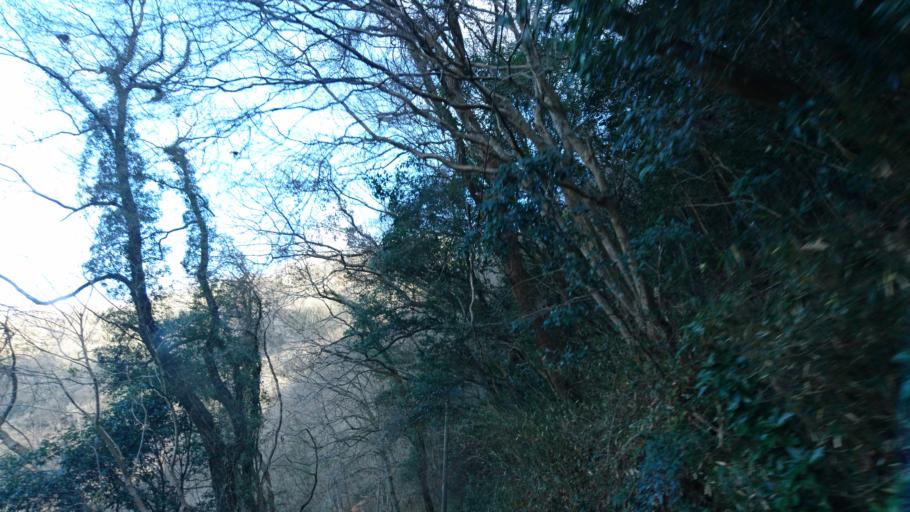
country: JP
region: Okayama
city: Takahashi
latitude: 34.8580
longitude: 133.5723
